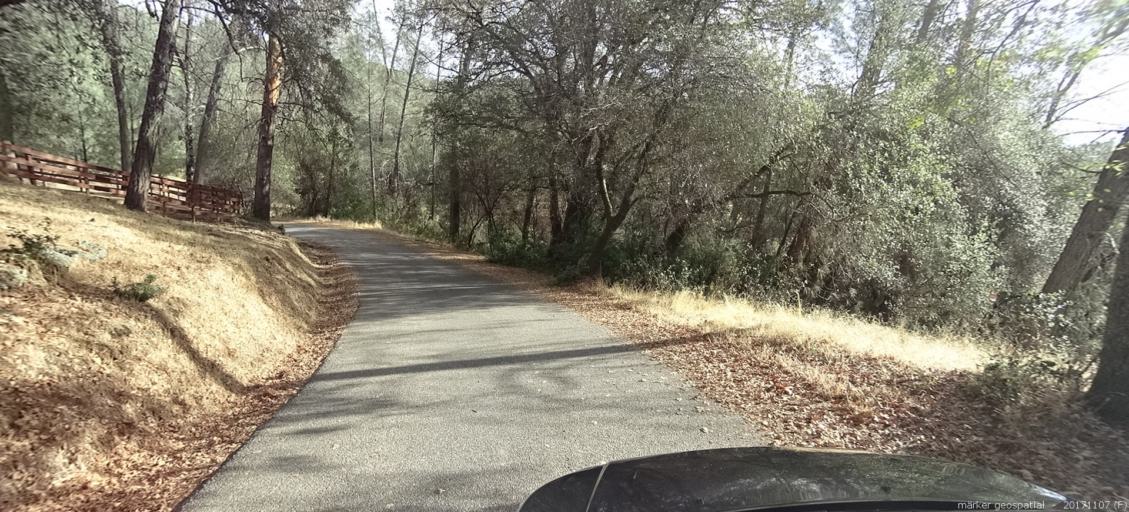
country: US
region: California
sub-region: Shasta County
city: Shasta
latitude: 40.5359
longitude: -122.5278
